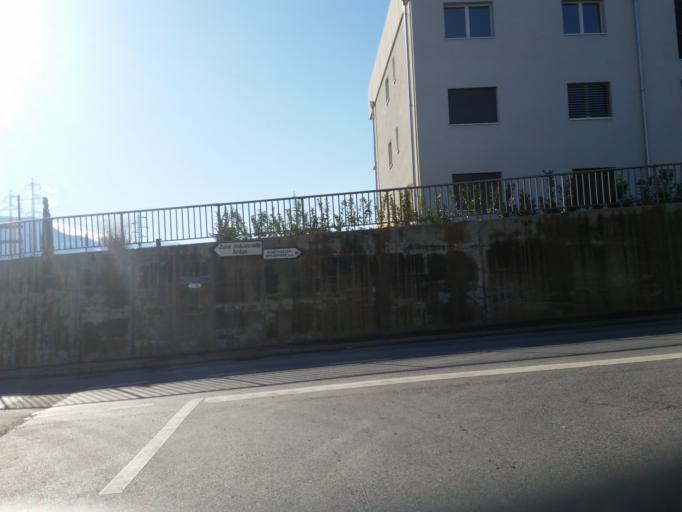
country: CH
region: Valais
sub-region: Conthey District
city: Ardon
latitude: 46.2078
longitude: 7.2688
